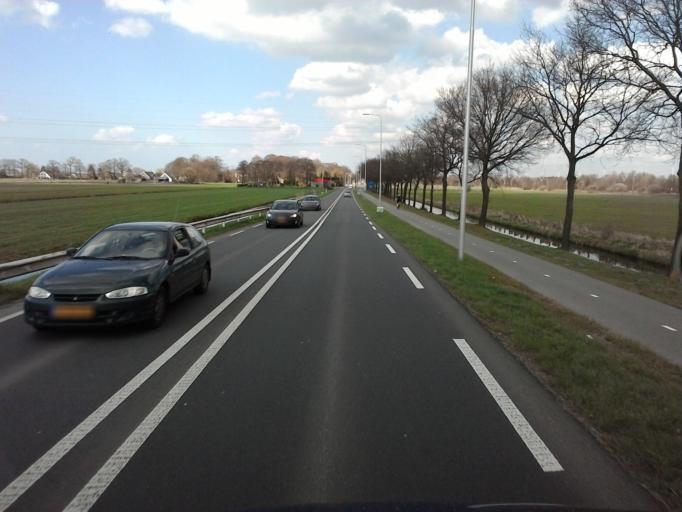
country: NL
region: Utrecht
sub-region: Gemeente De Bilt
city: De Bilt
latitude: 52.1446
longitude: 5.1566
